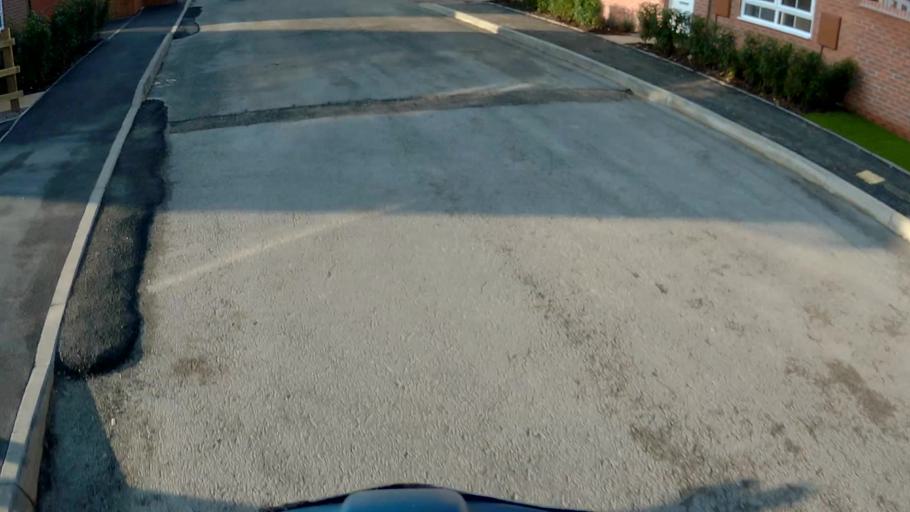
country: GB
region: England
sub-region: Lincolnshire
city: Bourne
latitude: 52.7589
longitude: -0.3882
